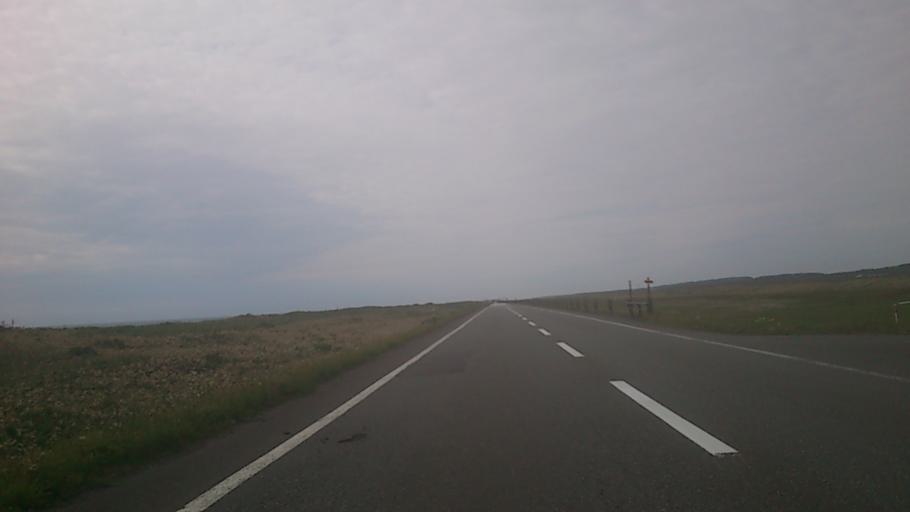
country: JP
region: Hokkaido
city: Wakkanai
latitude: 45.0567
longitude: 141.6494
